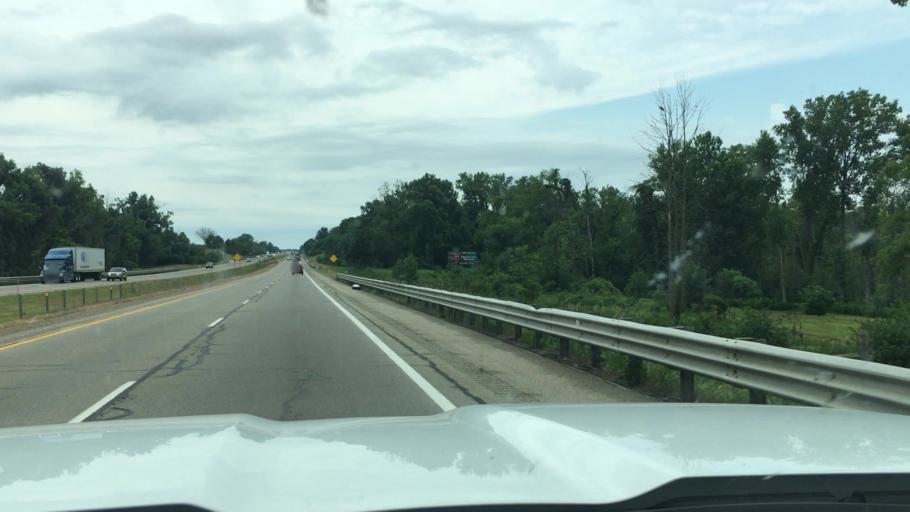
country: US
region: Michigan
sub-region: Allegan County
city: Wayland
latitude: 42.5699
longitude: -85.6626
